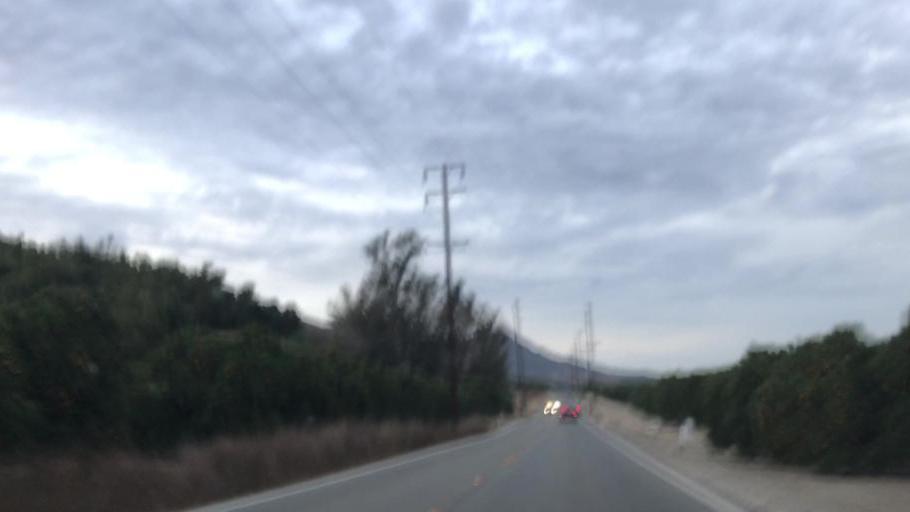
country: US
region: California
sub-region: Ventura County
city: Fillmore
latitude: 34.3593
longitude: -118.9572
